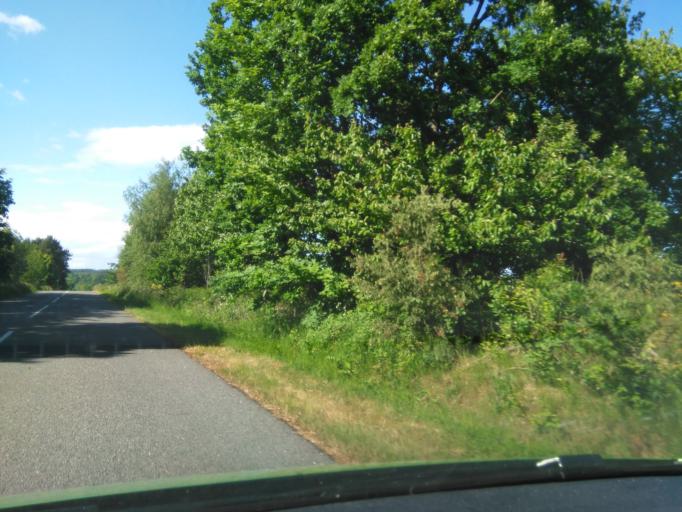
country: DK
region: Capital Region
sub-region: Bornholm Kommune
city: Nexo
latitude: 55.0710
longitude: 15.0820
